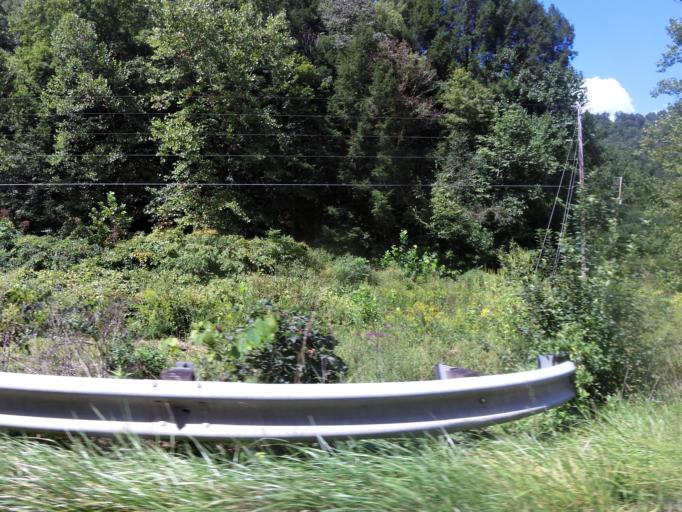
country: US
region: Kentucky
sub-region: Harlan County
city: Loyall
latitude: 36.9547
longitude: -83.3906
